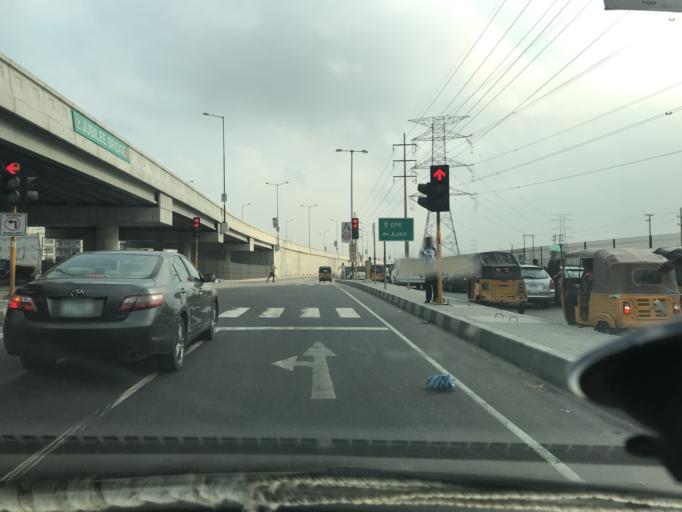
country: NG
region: Lagos
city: Ikoyi
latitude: 6.4678
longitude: 3.5655
